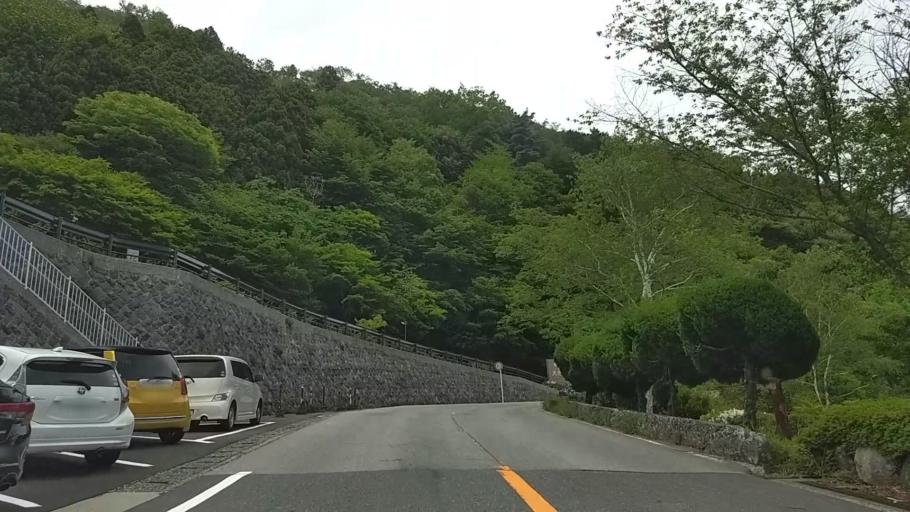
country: JP
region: Kanagawa
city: Hakone
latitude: 35.2395
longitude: 139.0441
